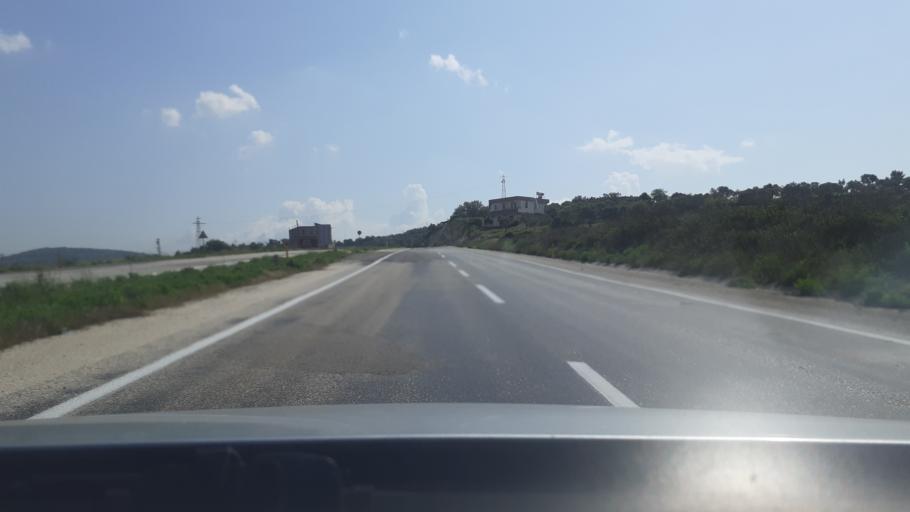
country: TR
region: Hatay
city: Harbiye
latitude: 36.1143
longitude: 36.1631
